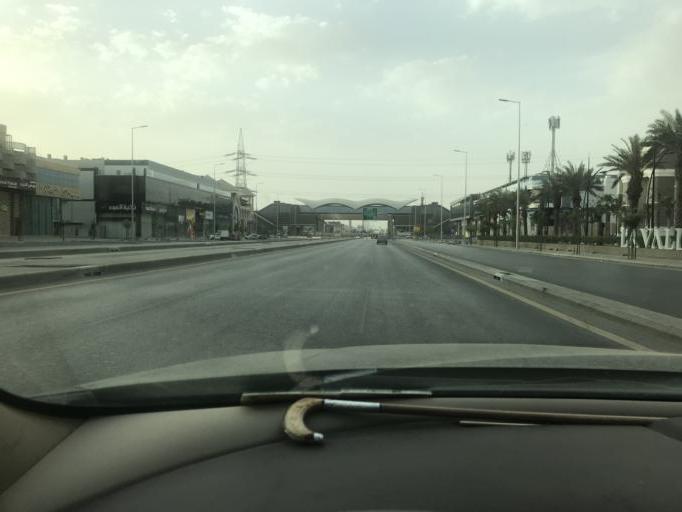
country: SA
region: Ar Riyad
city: Riyadh
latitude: 24.7831
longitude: 46.6619
